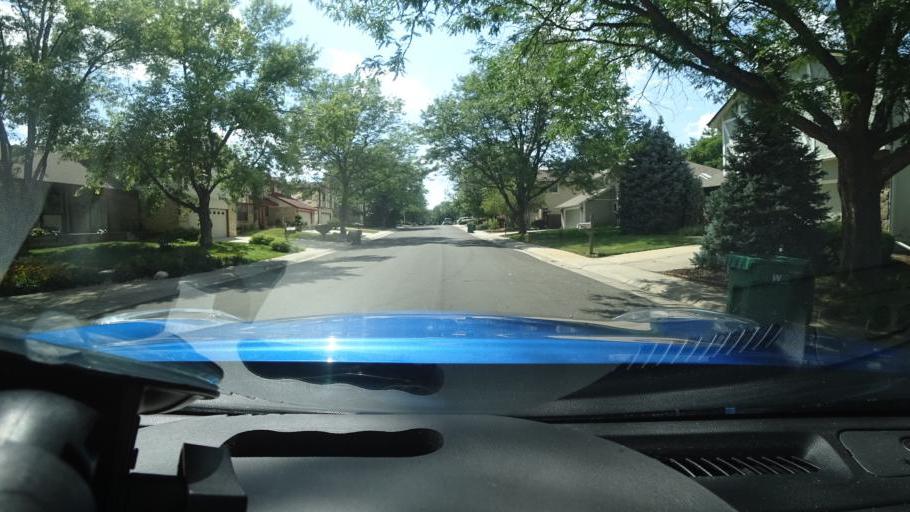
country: US
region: Colorado
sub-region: Adams County
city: Aurora
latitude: 39.6770
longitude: -104.8513
